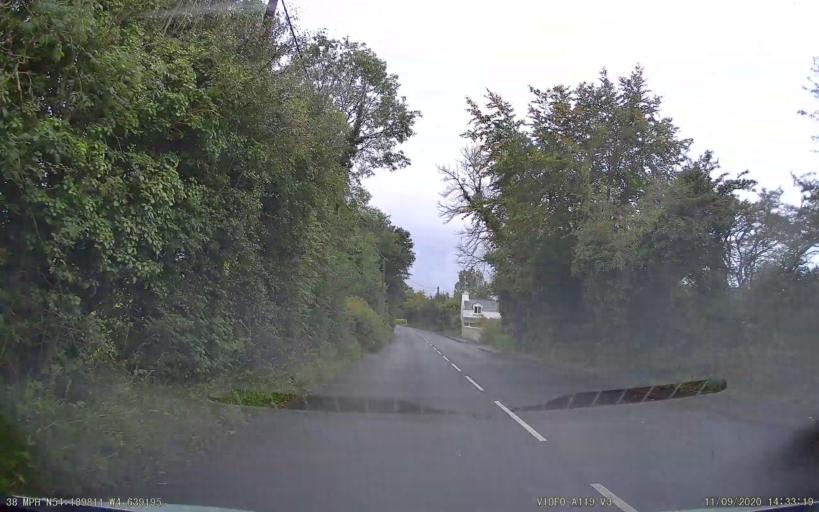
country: IM
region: Castletown
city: Castletown
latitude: 54.1898
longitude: -4.6392
